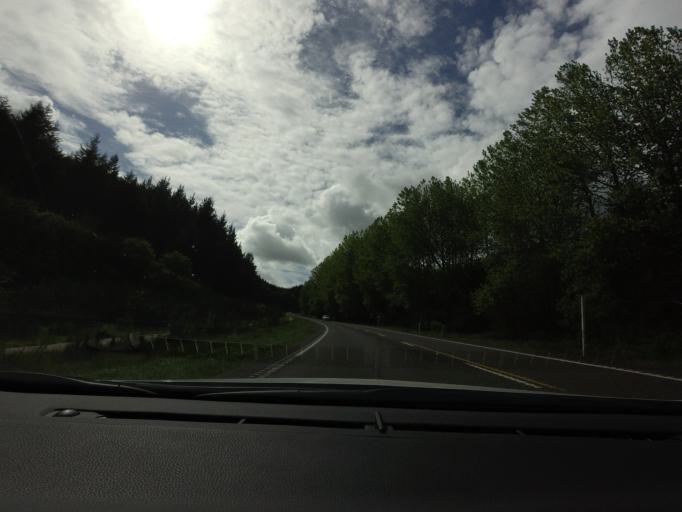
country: NZ
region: Bay of Plenty
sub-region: Rotorua District
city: Rotorua
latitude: -38.2271
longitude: 176.2928
